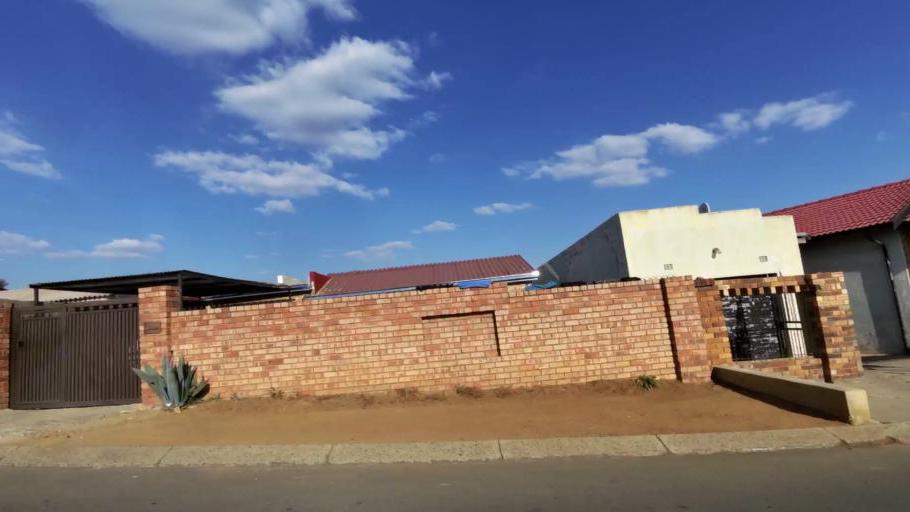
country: ZA
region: Gauteng
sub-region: City of Johannesburg Metropolitan Municipality
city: Roodepoort
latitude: -26.2029
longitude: 27.8792
